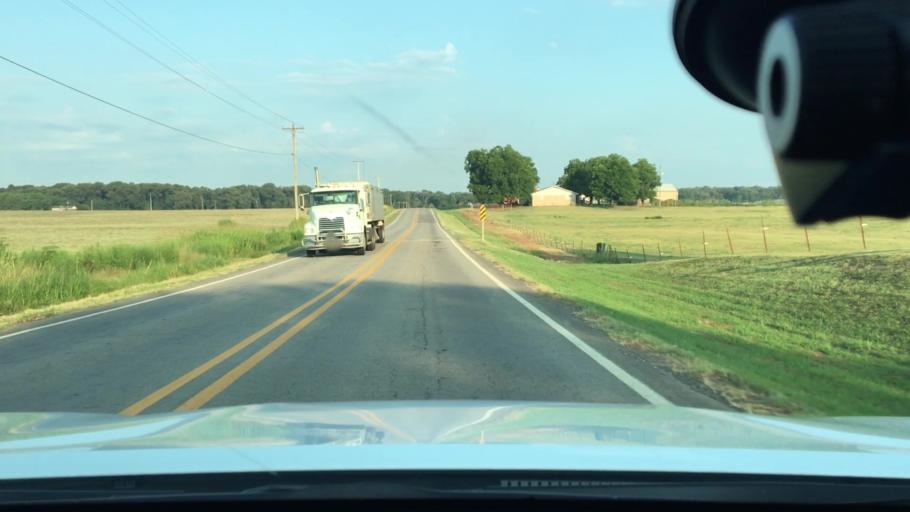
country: US
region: Arkansas
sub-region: Johnson County
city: Clarksville
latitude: 35.3792
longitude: -93.5528
